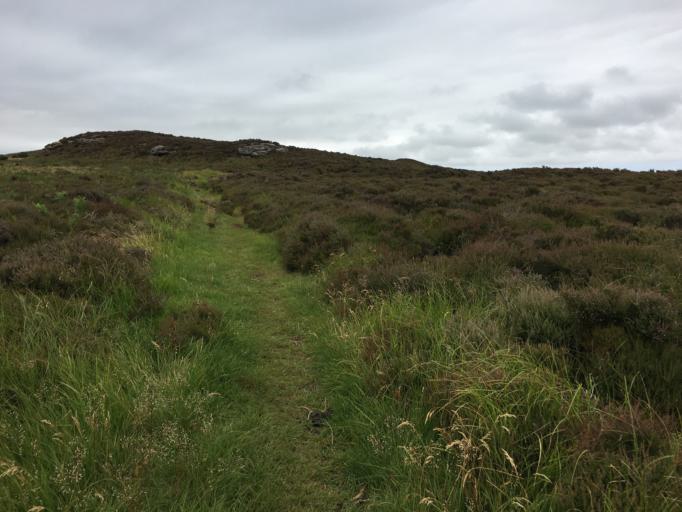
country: GB
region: England
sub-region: Northumberland
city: Lowick
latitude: 55.6142
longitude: -1.9107
